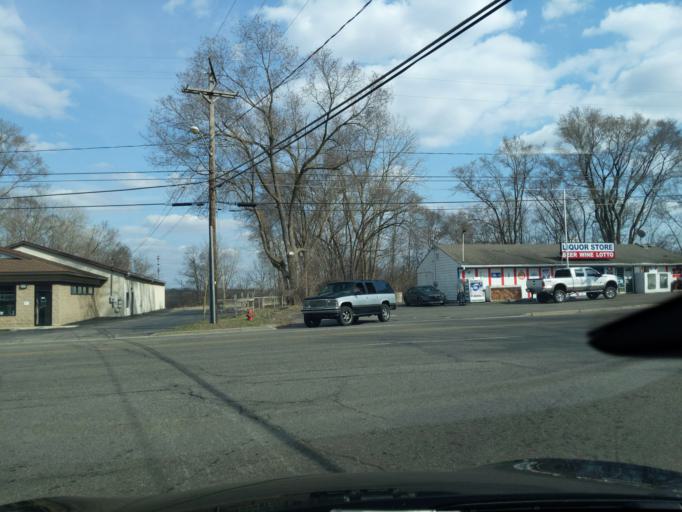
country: US
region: Michigan
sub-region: Jackson County
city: Jackson
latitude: 42.2736
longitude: -84.4148
